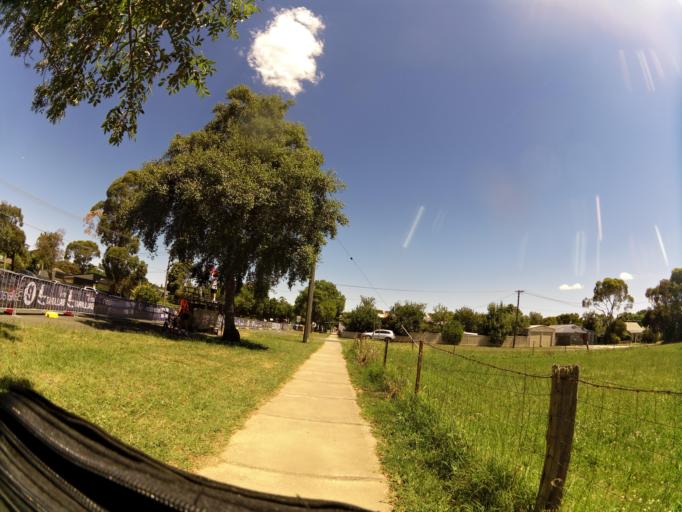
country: AU
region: Victoria
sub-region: Ballarat North
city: Mount Clear
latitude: -37.6463
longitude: 143.8851
